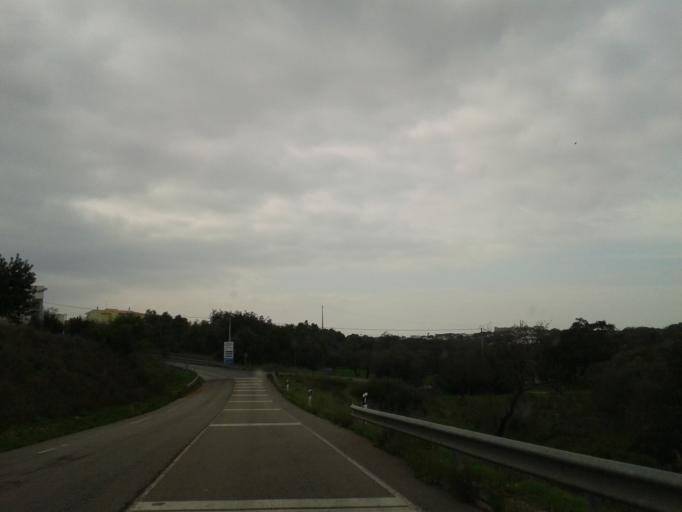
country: PT
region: Faro
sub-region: Loule
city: Boliqueime
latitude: 37.1128
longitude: -8.1865
